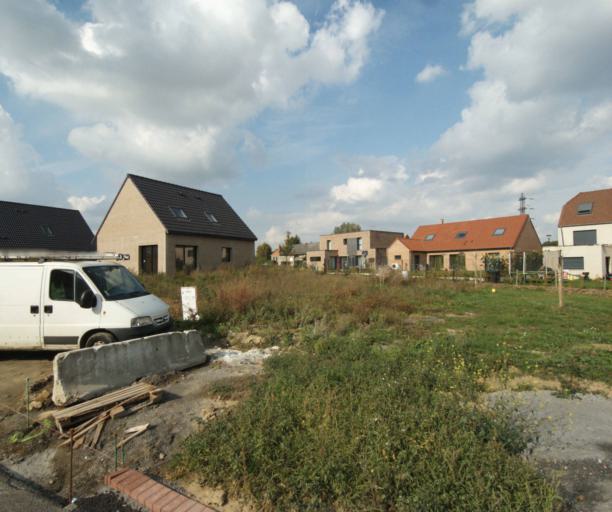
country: FR
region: Nord-Pas-de-Calais
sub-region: Departement du Nord
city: Hallennes-lez-Haubourdin
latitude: 50.6168
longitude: 2.9584
